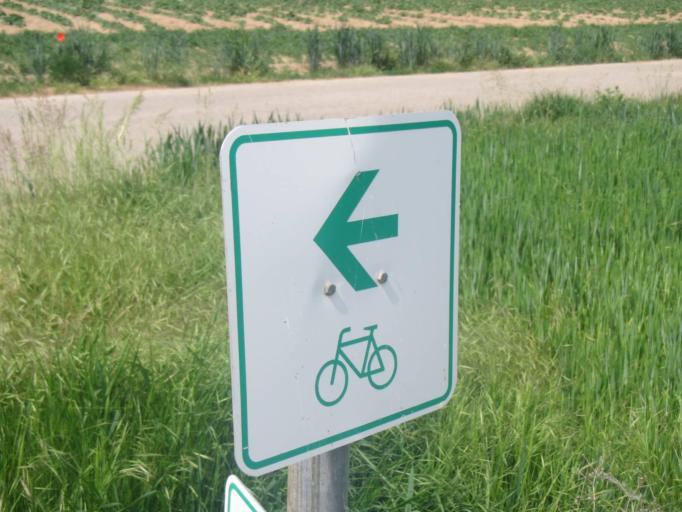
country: DE
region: Rheinland-Pfalz
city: Insheim
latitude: 49.1575
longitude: 8.1806
